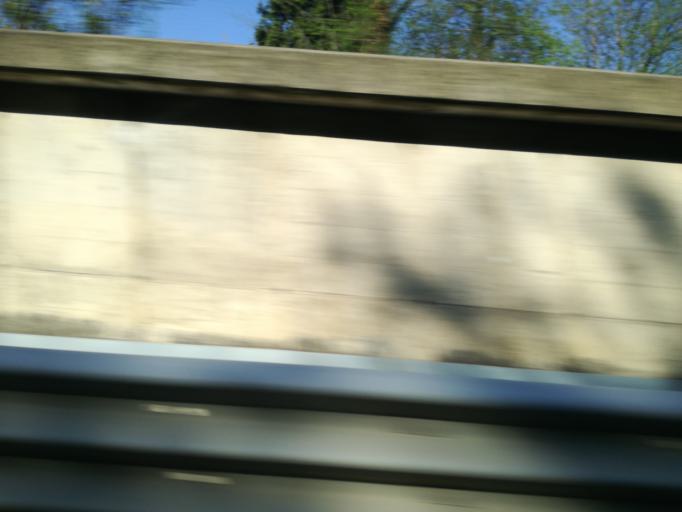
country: IT
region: Lombardy
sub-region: Provincia di Bergamo
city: Carvico
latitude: 45.7016
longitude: 9.4738
